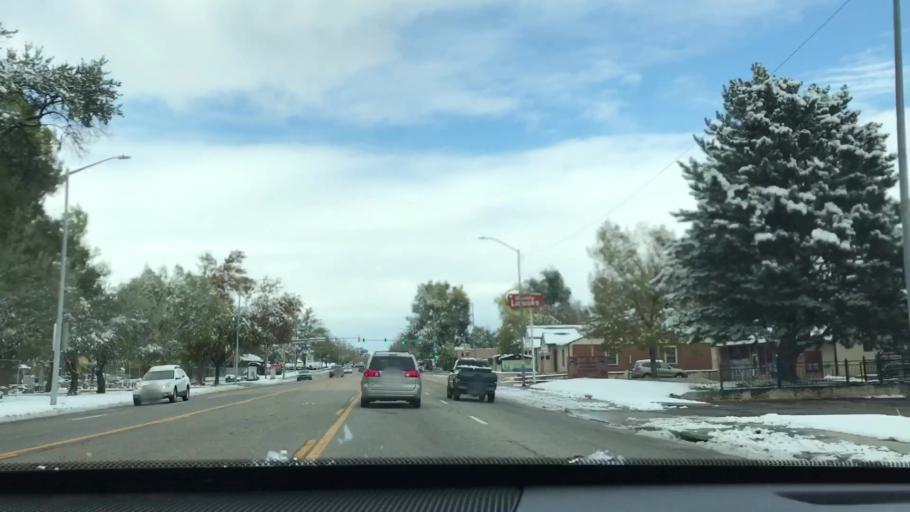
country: US
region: Colorado
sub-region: Boulder County
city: Longmont
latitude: 40.1799
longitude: -105.1024
